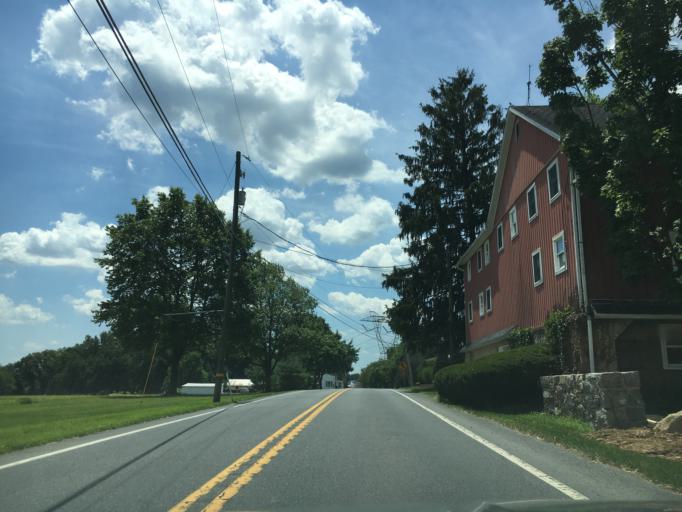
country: US
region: Pennsylvania
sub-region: Lehigh County
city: Schnecksville
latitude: 40.6505
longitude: -75.5772
